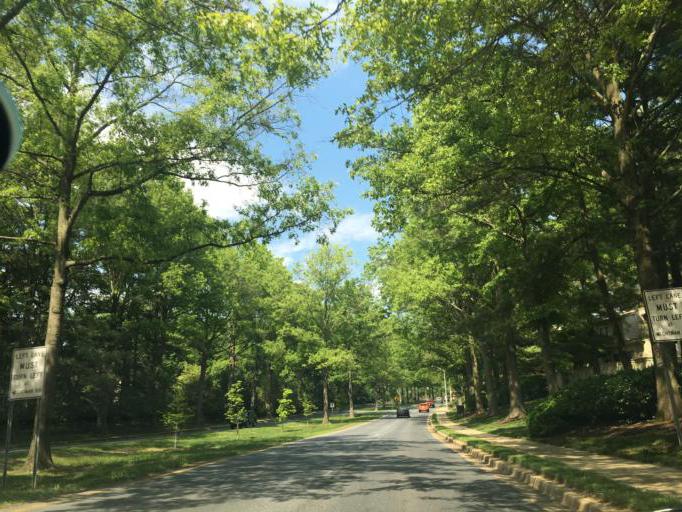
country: US
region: Maryland
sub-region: Montgomery County
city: Montgomery Village
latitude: 39.1894
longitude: -77.1950
